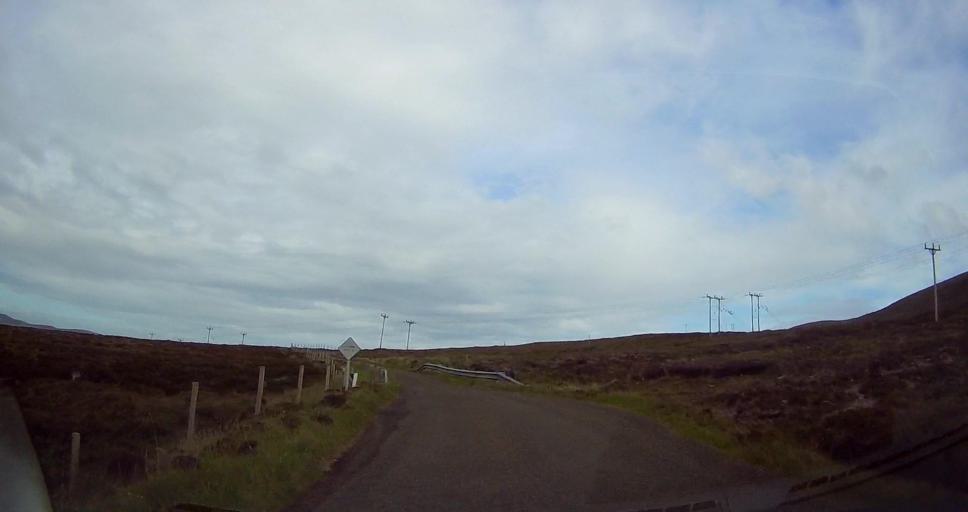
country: GB
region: Scotland
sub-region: Orkney Islands
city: Stromness
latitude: 58.9010
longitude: -3.2908
